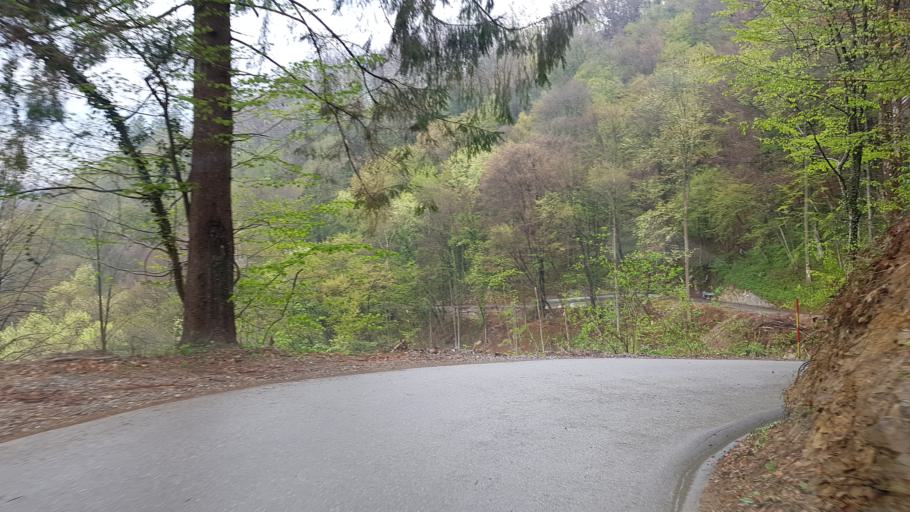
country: SI
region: Tolmin
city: Tolmin
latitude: 46.1460
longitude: 13.7809
